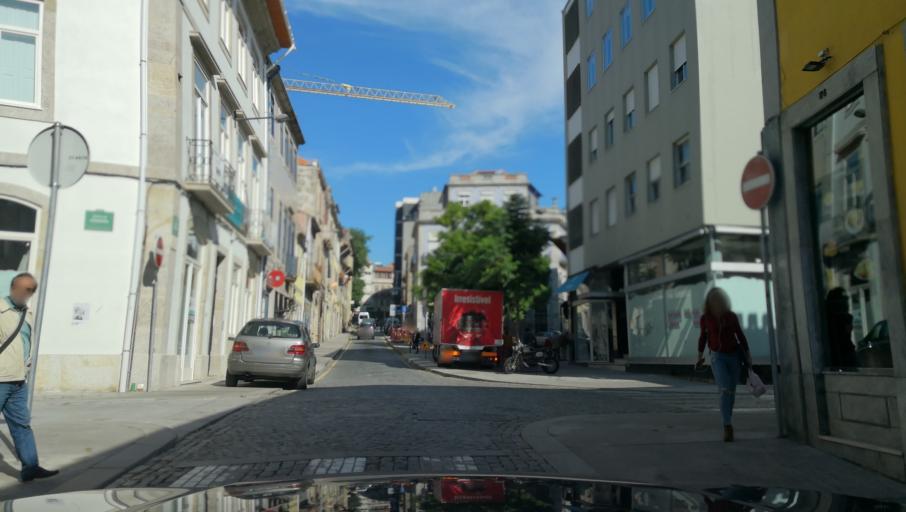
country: PT
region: Porto
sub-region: Porto
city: Porto
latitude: 41.1499
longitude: -8.6148
